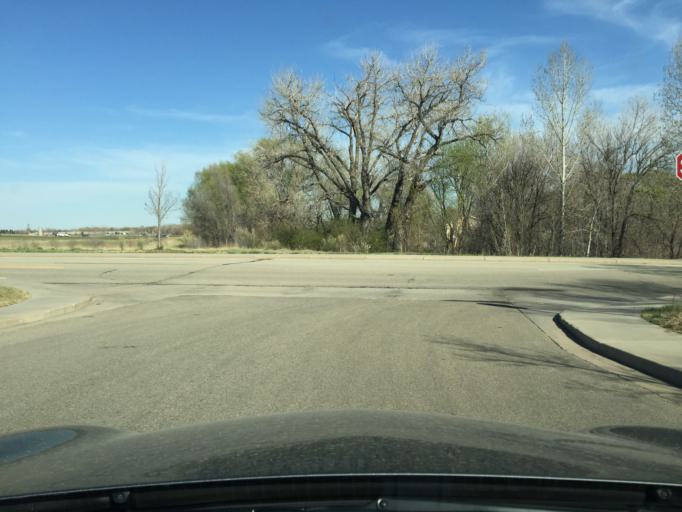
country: US
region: Colorado
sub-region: Boulder County
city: Niwot
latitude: 40.1345
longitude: -105.1416
